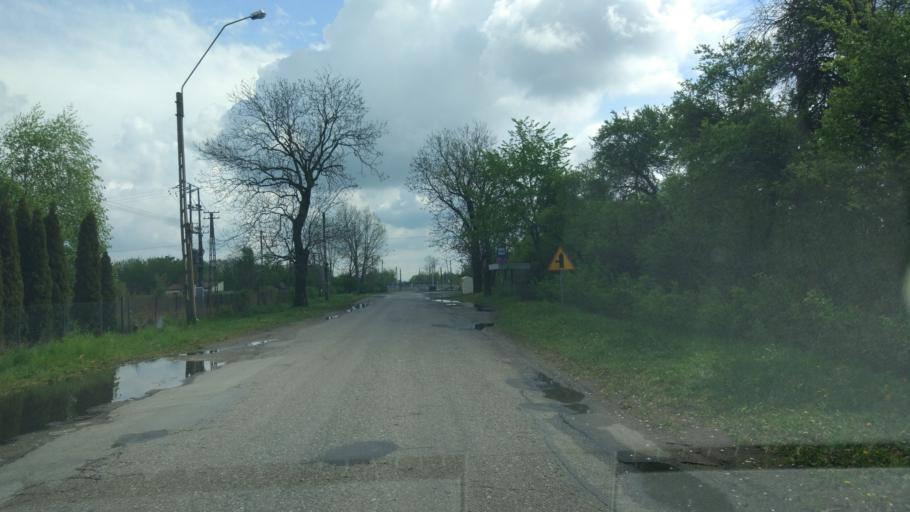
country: PL
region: Lodz Voivodeship
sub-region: Powiat kutnowski
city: Kutno
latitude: 52.2258
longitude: 19.4023
